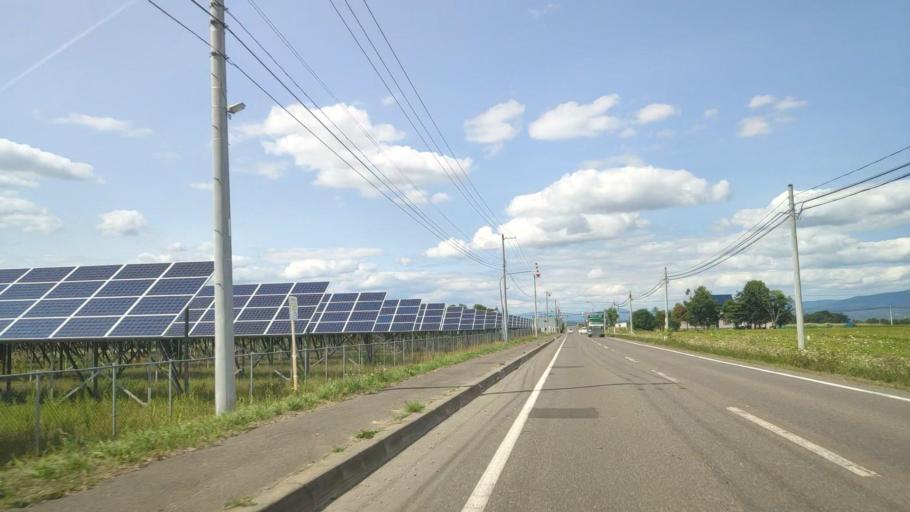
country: JP
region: Hokkaido
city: Nayoro
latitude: 44.2942
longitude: 142.4294
